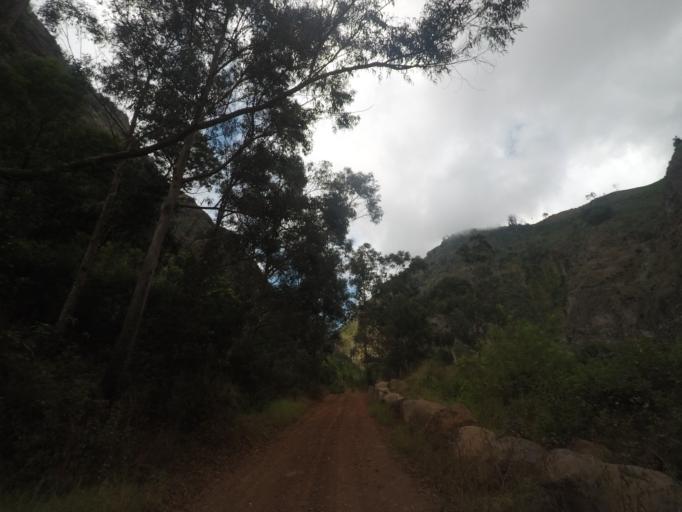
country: PT
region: Madeira
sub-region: Funchal
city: Nossa Senhora do Monte
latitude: 32.6914
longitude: -16.9174
